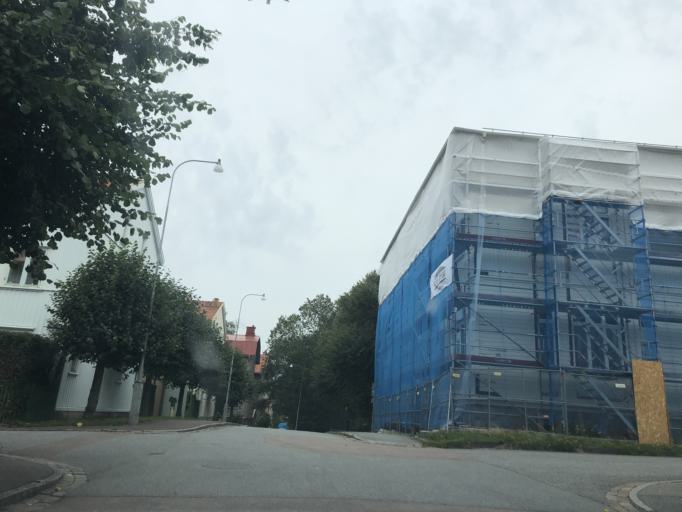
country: SE
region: Vaestra Goetaland
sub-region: Goteborg
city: Majorna
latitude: 57.7060
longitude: 11.9330
